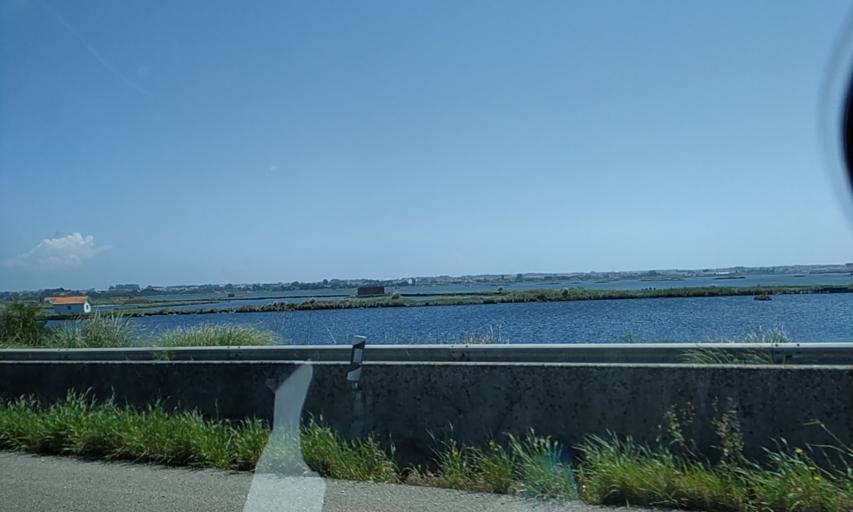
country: PT
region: Aveiro
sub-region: Ilhavo
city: Gafanha da Nazare
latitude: 40.6325
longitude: -8.6840
